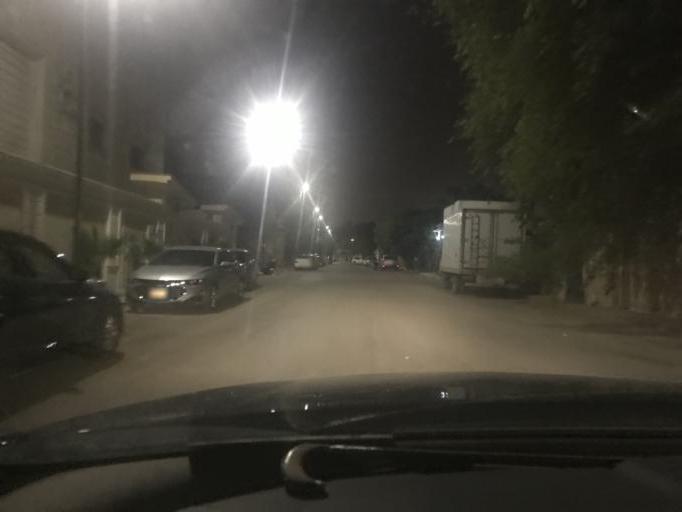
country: SA
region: Ar Riyad
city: Riyadh
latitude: 24.7256
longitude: 46.7636
